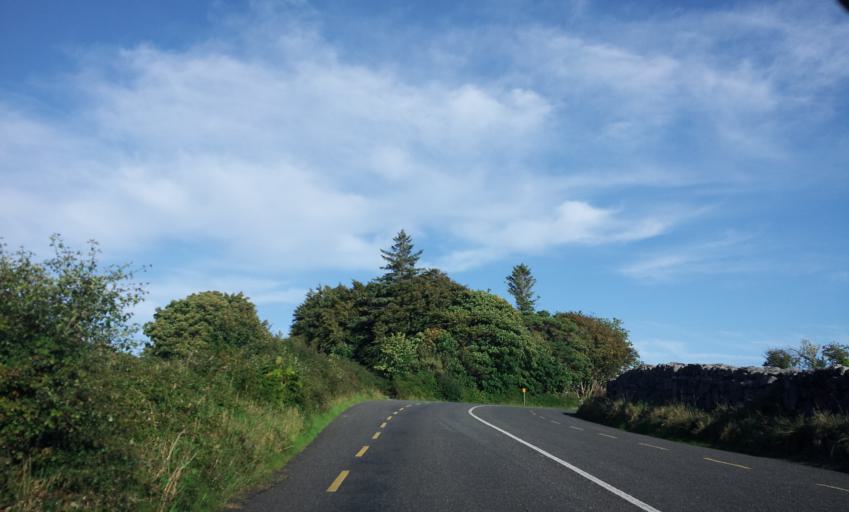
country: IE
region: Munster
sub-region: An Clar
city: Ennis
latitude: 52.9766
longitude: -9.1026
